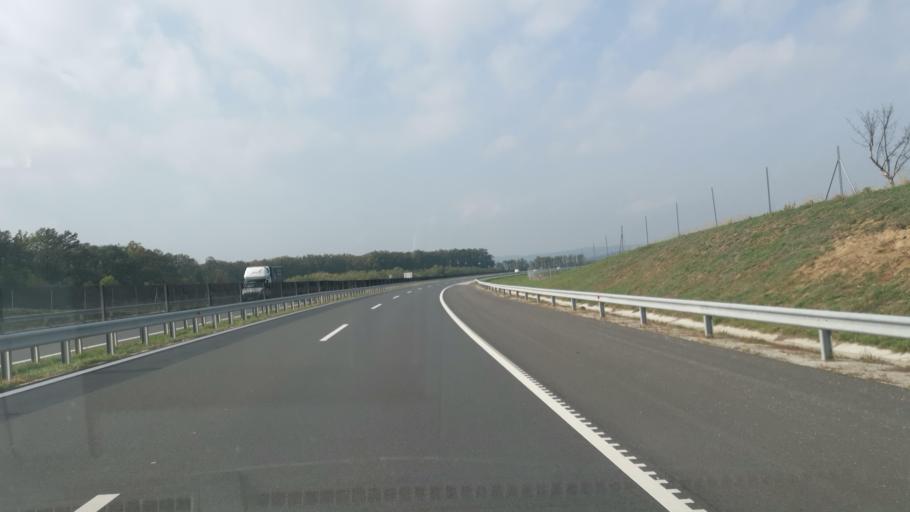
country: AT
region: Burgenland
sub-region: Politischer Bezirk Oberpullendorf
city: Deutschkreutz
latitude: 47.6295
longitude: 16.6366
